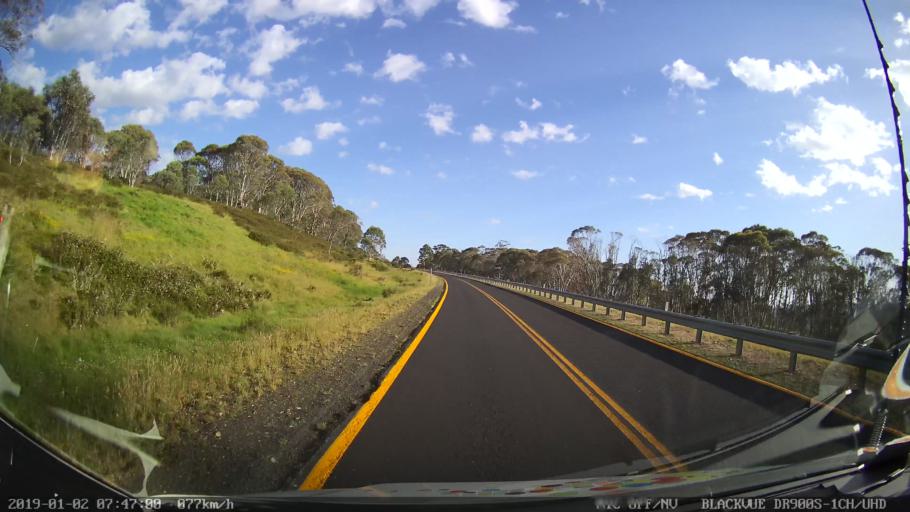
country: AU
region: New South Wales
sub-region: Tumut Shire
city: Tumut
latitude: -35.7696
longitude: 148.5214
